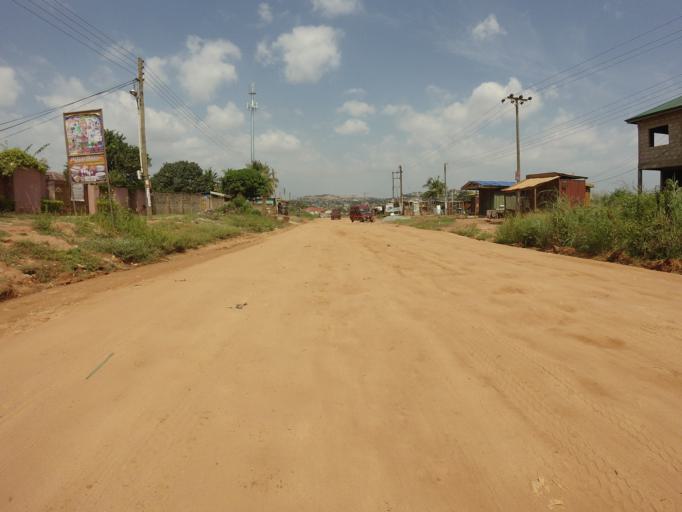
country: GH
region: Greater Accra
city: Gbawe
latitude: 5.6180
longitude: -0.3102
